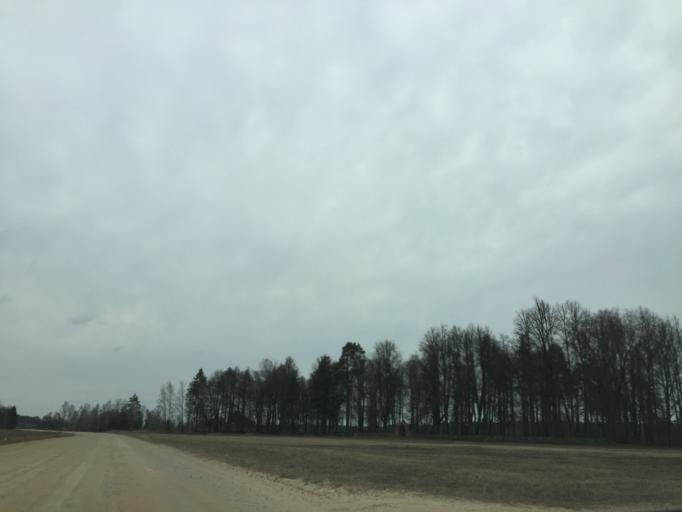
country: LV
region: Livani
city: Livani
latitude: 56.3023
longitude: 26.1709
